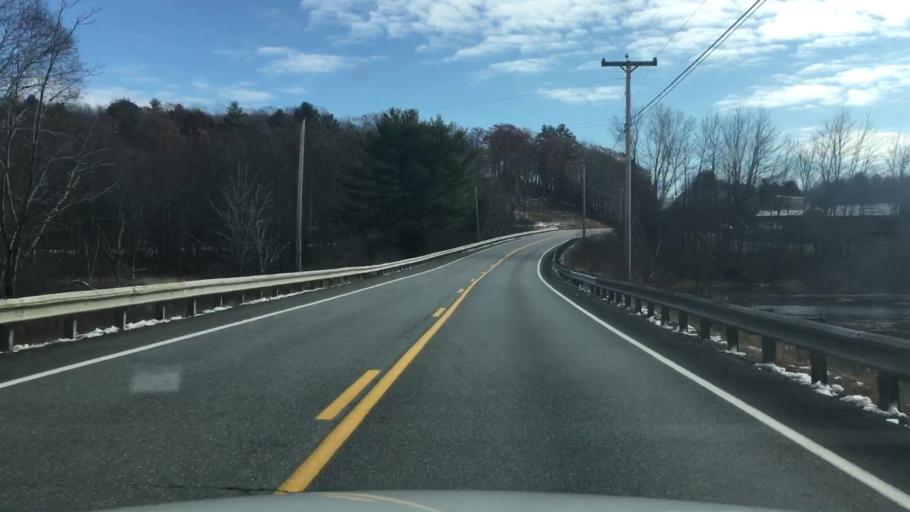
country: US
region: Maine
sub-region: Kennebec County
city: Wayne
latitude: 44.3382
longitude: -70.0179
